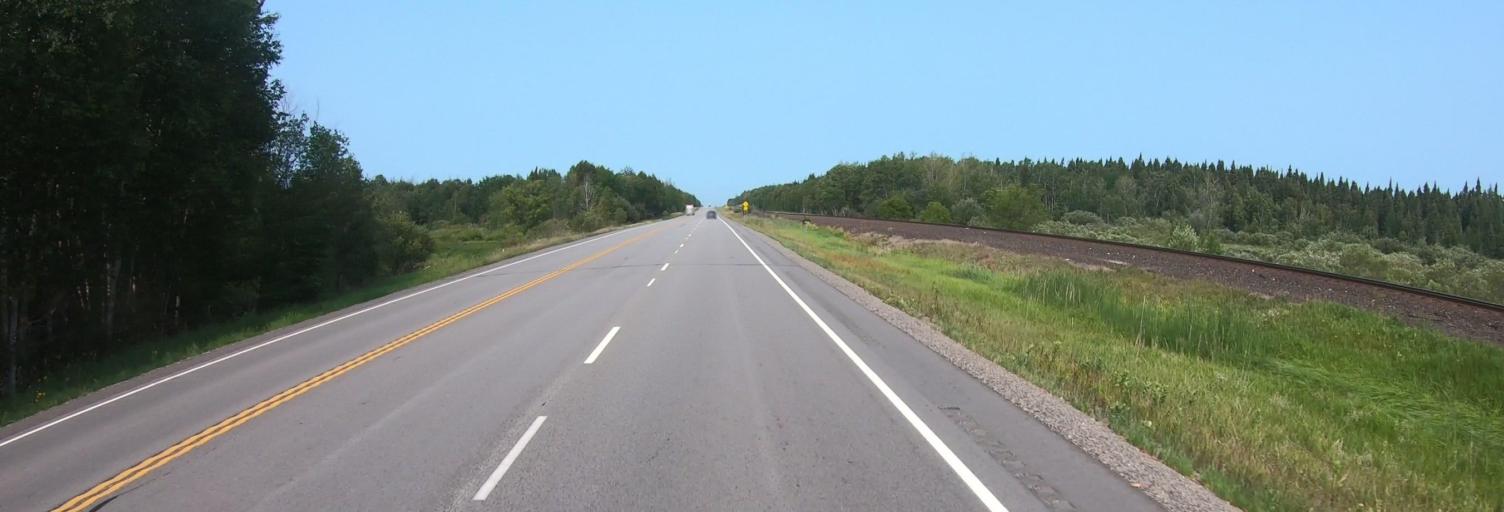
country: CA
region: Ontario
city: Fort Frances
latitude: 48.4561
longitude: -93.2791
